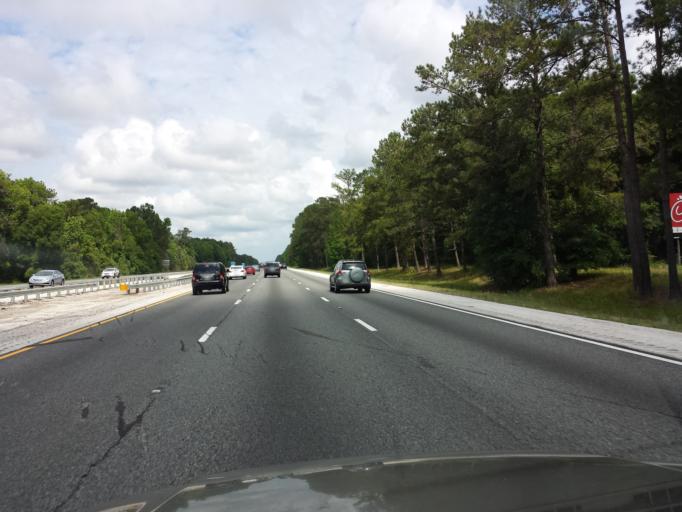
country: US
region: Florida
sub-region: Marion County
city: Citra
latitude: 29.4688
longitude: -82.2745
